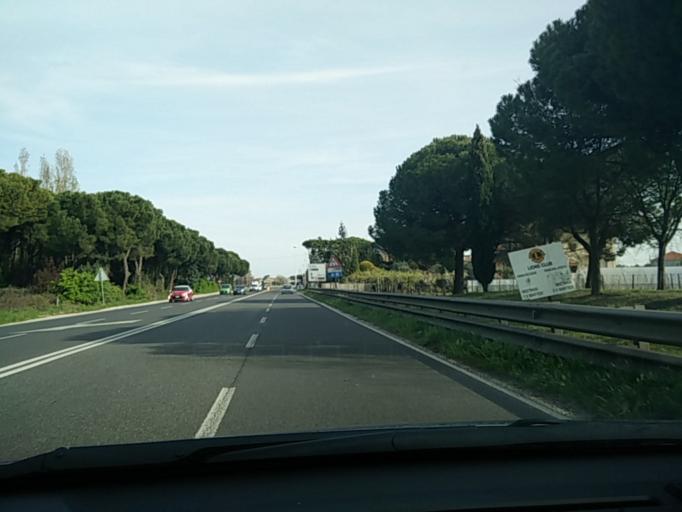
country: IT
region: Emilia-Romagna
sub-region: Provincia di Rimini
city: Rimini
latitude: 44.0764
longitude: 12.5344
